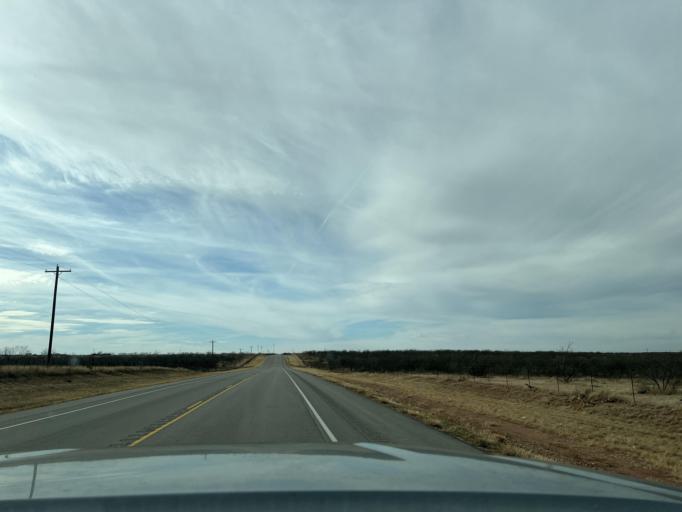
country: US
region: Texas
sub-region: Jones County
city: Anson
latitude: 32.7506
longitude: -99.6933
